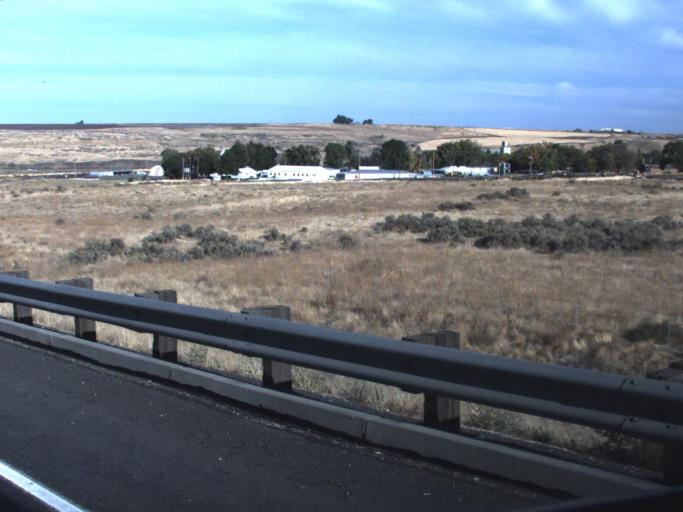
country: US
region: Washington
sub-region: Franklin County
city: Basin City
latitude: 46.5689
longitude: -118.9992
